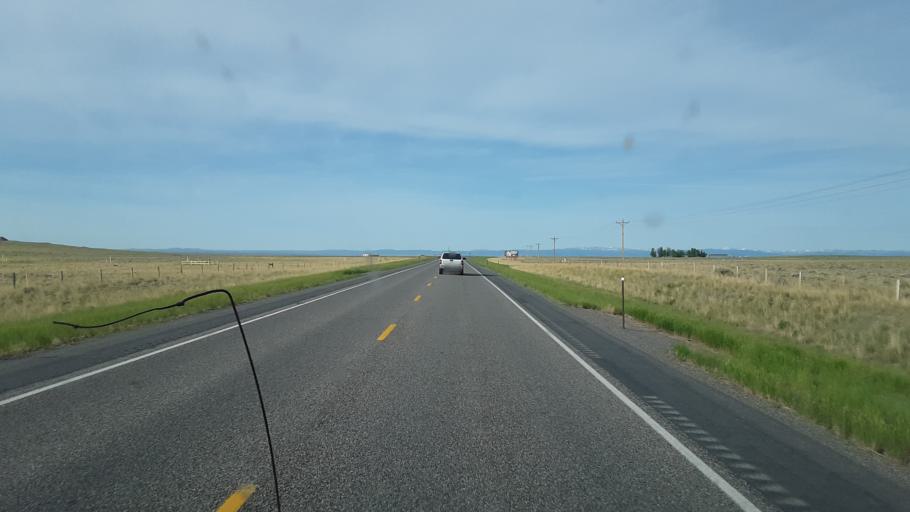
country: US
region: Wyoming
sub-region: Fremont County
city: Riverton
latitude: 43.1564
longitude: -108.2736
